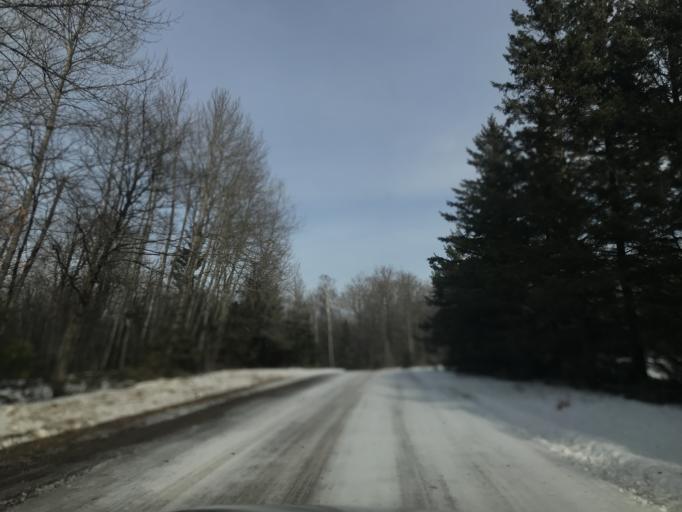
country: US
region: Wisconsin
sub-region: Door County
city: Sturgeon Bay
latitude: 45.1497
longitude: -87.0542
